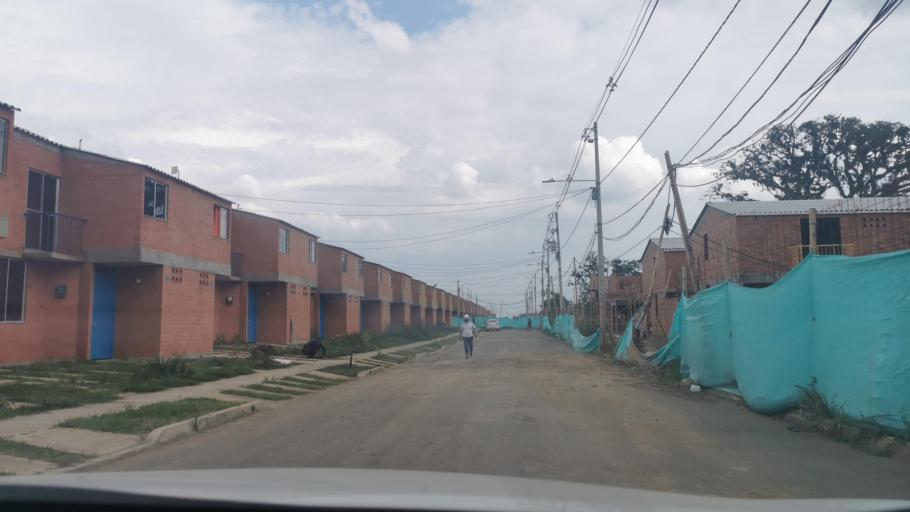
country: CO
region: Valle del Cauca
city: Jamundi
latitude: 3.2330
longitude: -76.5262
